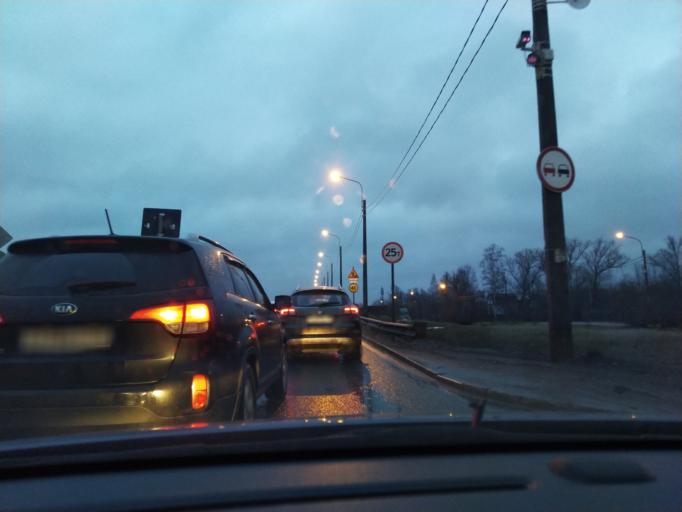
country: RU
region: St.-Petersburg
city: Uritsk
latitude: 59.8202
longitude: 30.1809
